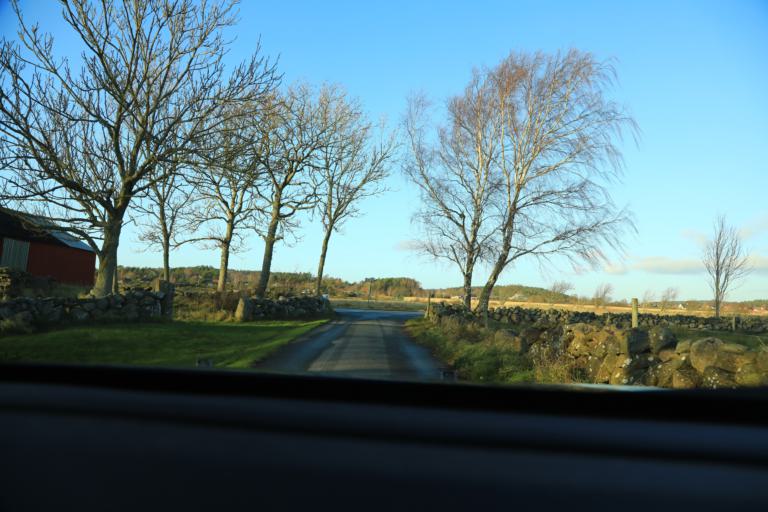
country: SE
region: Halland
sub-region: Varbergs Kommun
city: Varberg
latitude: 57.1648
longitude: 12.2226
